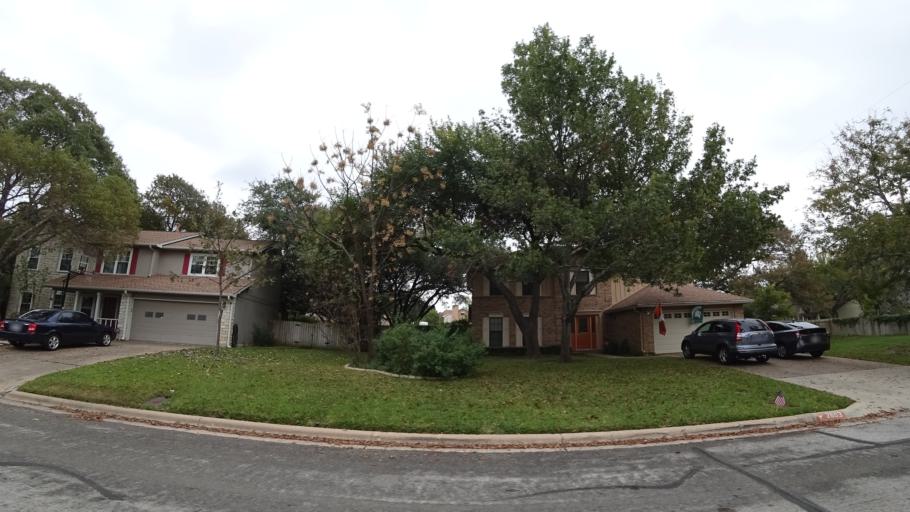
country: US
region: Texas
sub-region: Williamson County
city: Round Rock
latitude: 30.4857
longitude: -97.7039
